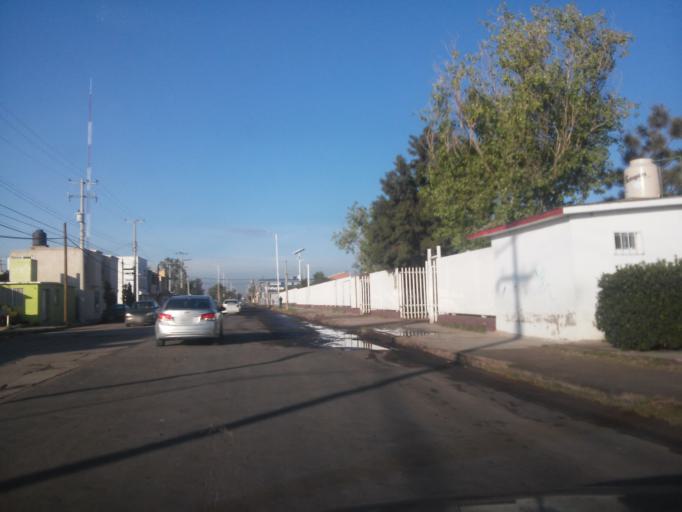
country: MX
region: Durango
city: Victoria de Durango
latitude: 24.0507
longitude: -104.6103
